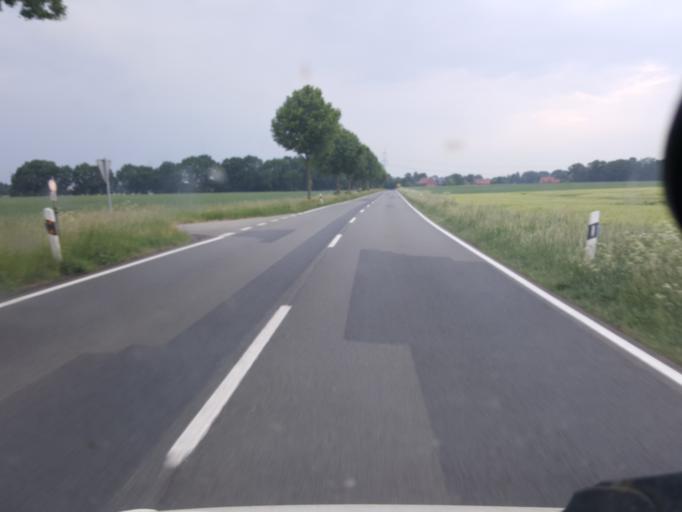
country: DE
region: Lower Saxony
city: Raddestorf
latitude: 52.4690
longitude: 8.9815
